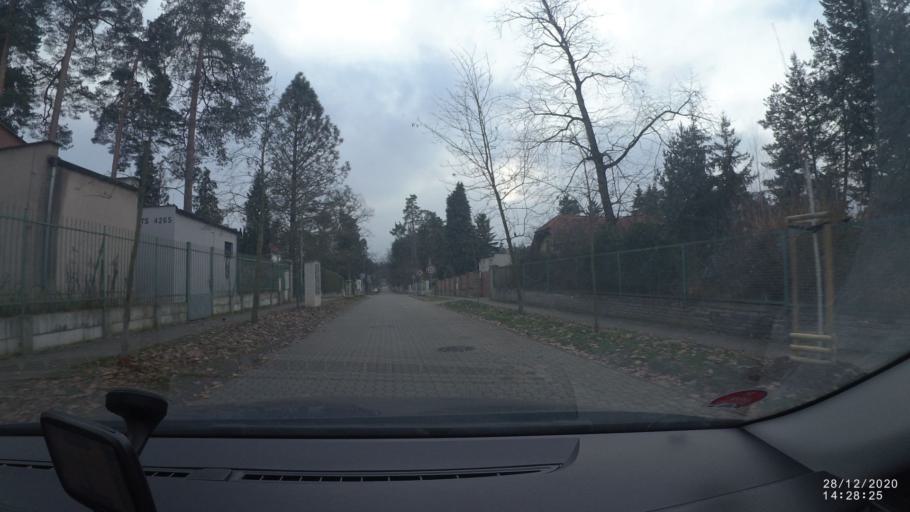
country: CZ
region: Central Bohemia
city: Sestajovice
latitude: 50.0910
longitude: 14.6650
